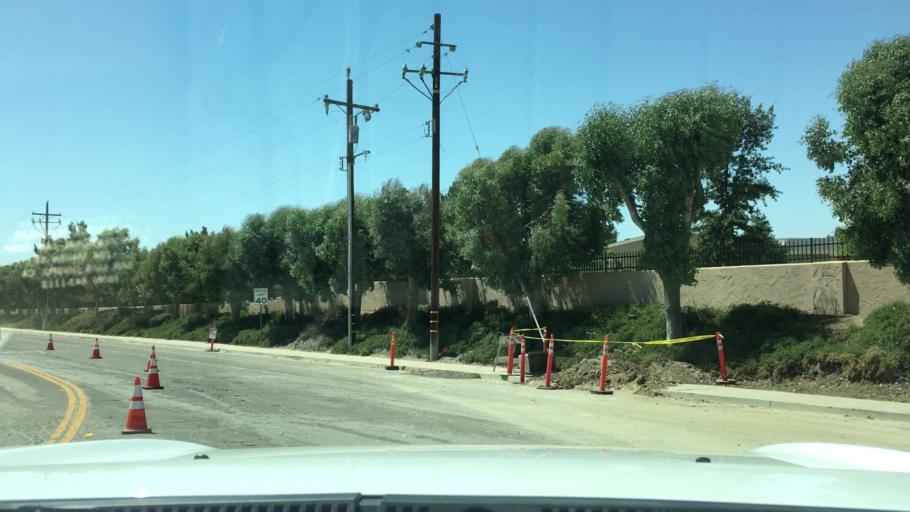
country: US
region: California
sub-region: San Luis Obispo County
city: Paso Robles
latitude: 35.6157
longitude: -120.6504
